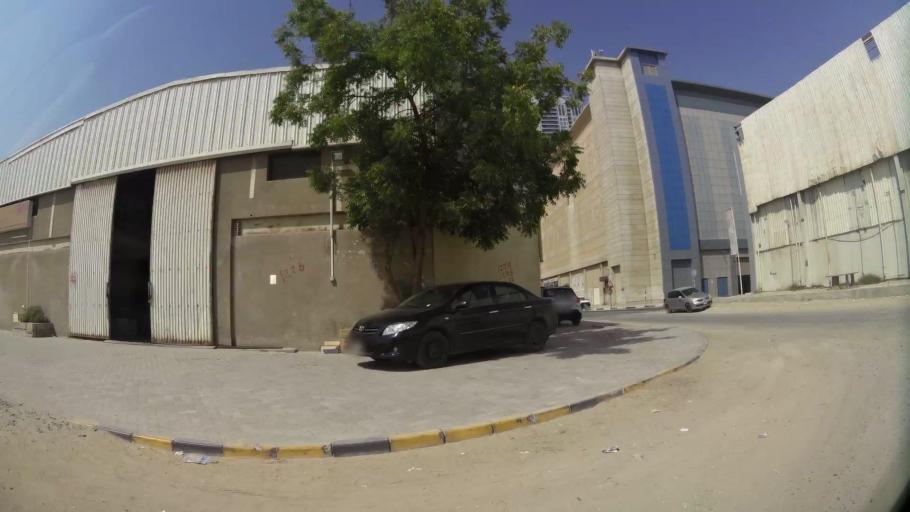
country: AE
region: Ash Shariqah
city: Sharjah
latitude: 25.3098
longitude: 55.3801
